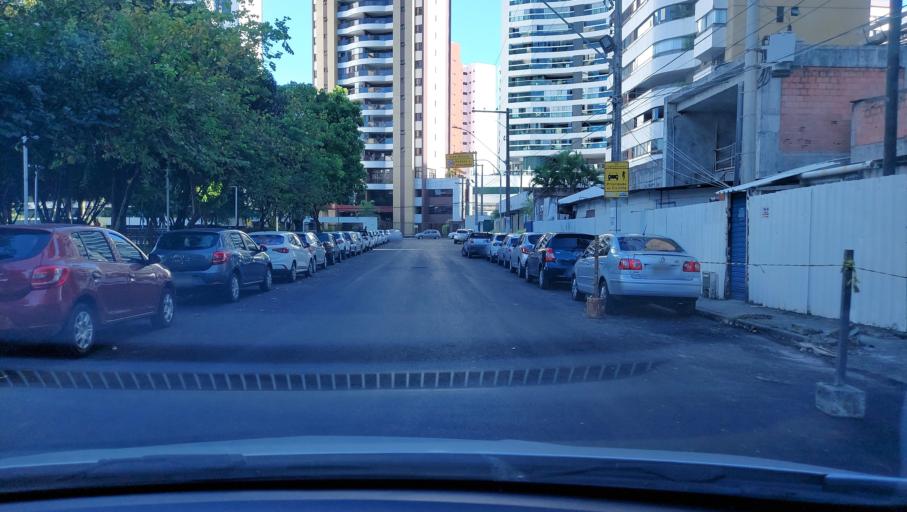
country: BR
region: Bahia
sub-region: Salvador
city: Salvador
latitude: -12.9871
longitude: -38.4526
